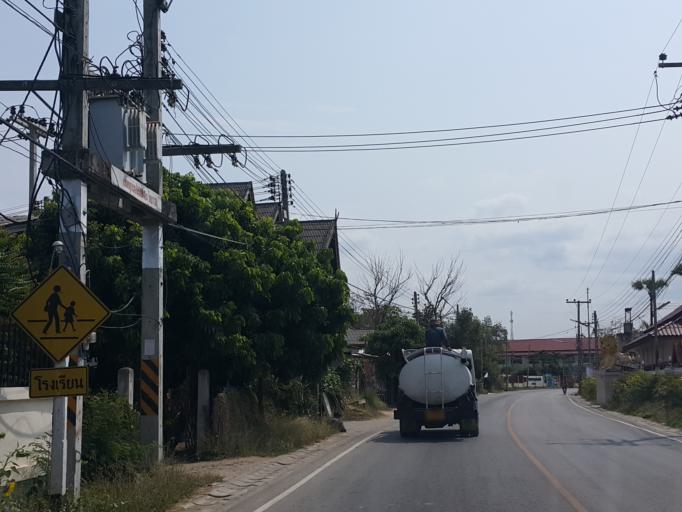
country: TH
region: Lamphun
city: Ban Thi
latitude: 18.6540
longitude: 99.1204
